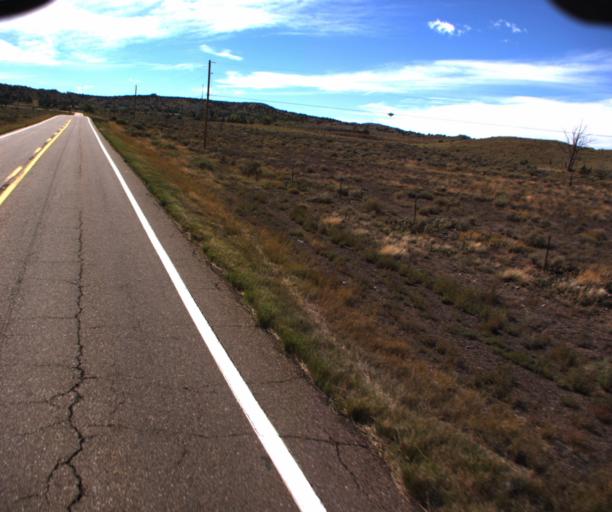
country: US
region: Arizona
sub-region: Apache County
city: Saint Johns
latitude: 34.4717
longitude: -109.6095
